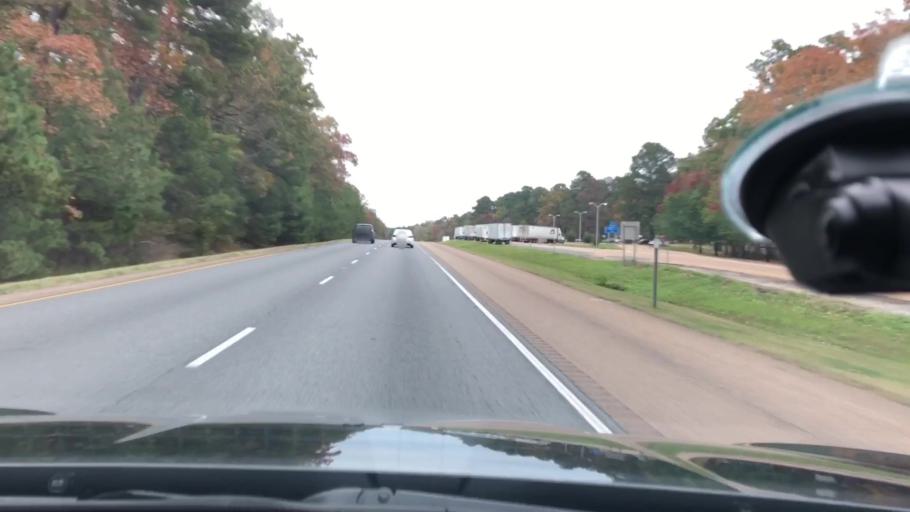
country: US
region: Arkansas
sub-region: Clark County
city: Gurdon
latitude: 33.9284
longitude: -93.2623
